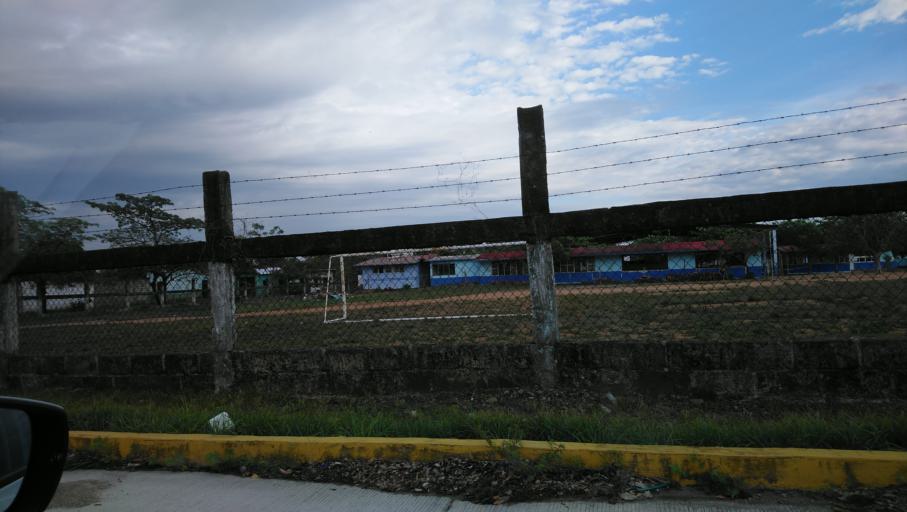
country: MX
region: Oaxaca
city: Chahuite
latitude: 16.3042
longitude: -94.1928
